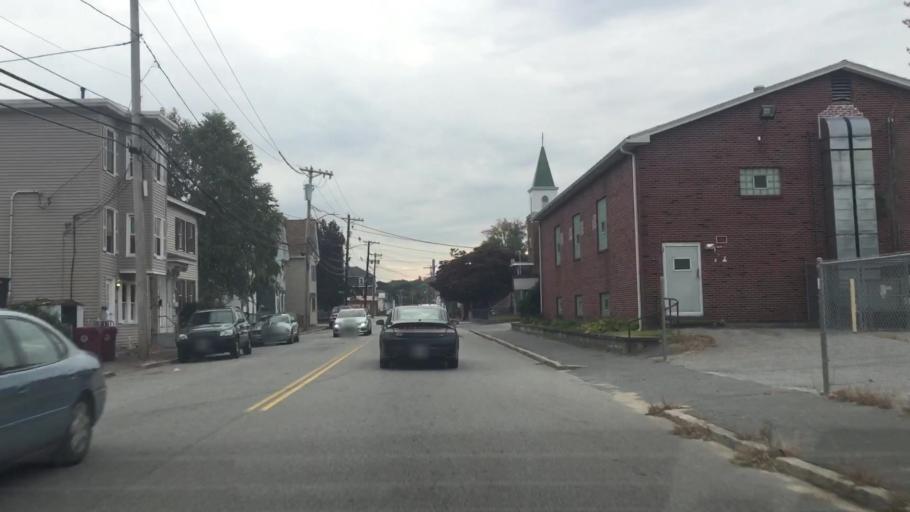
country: US
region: Massachusetts
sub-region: Middlesex County
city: Dracut
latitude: 42.6519
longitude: -71.3090
